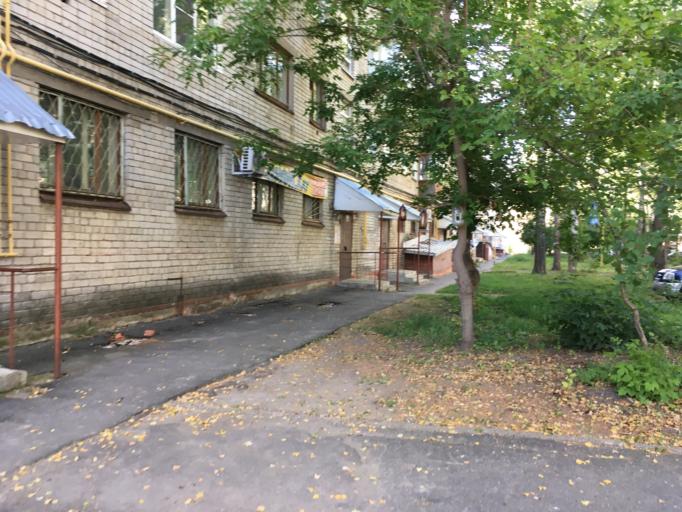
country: RU
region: Mariy-El
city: Yoshkar-Ola
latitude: 56.6449
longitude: 47.8664
